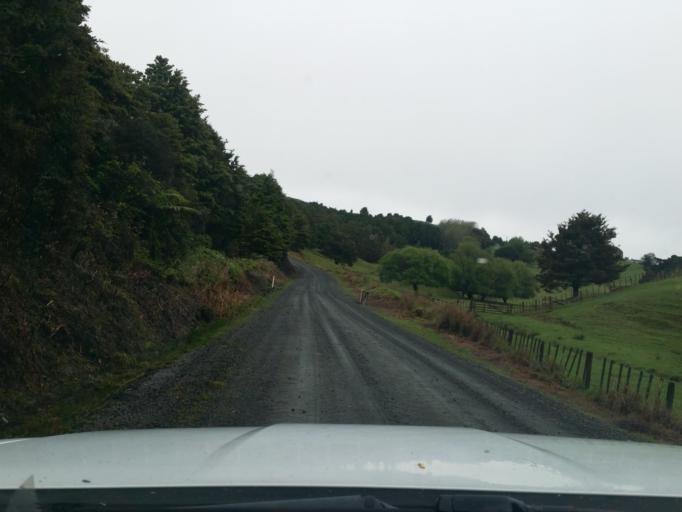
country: NZ
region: Northland
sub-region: Kaipara District
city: Dargaville
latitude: -35.7628
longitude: 173.9359
